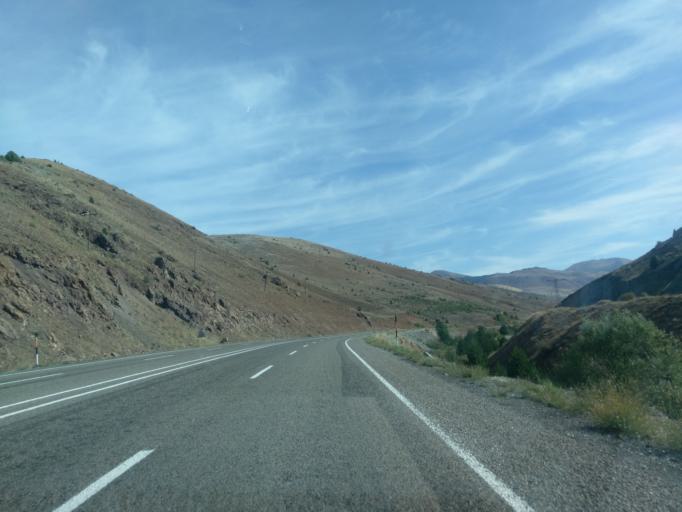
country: TR
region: Sivas
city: Imranli
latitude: 39.8528
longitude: 38.2975
